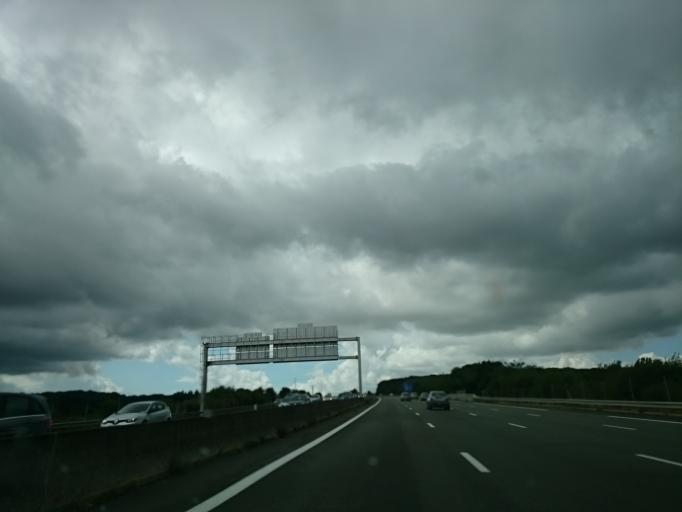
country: FR
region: Pays de la Loire
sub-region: Departement de la Sarthe
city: Saint-Saturnin
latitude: 48.0500
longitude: 0.1652
